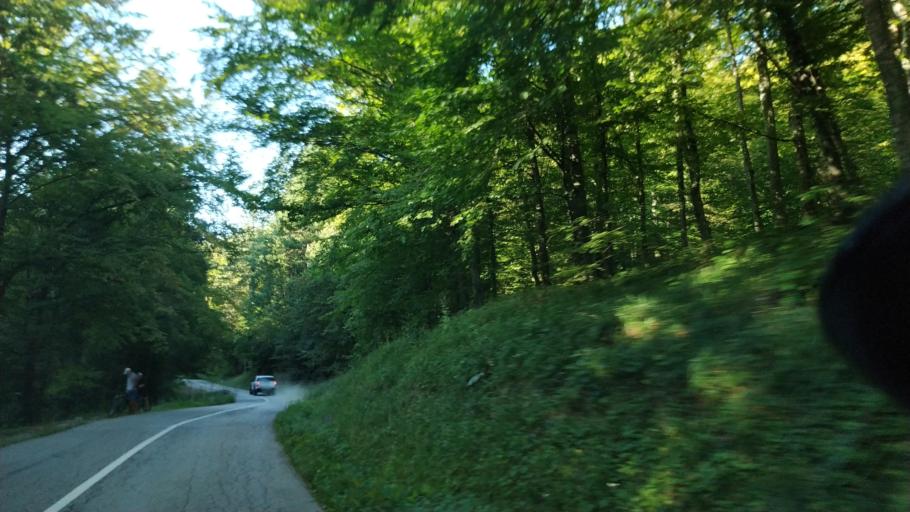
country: RS
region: Central Serbia
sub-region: Rasinski Okrug
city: Krusevac
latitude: 43.4516
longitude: 21.3595
